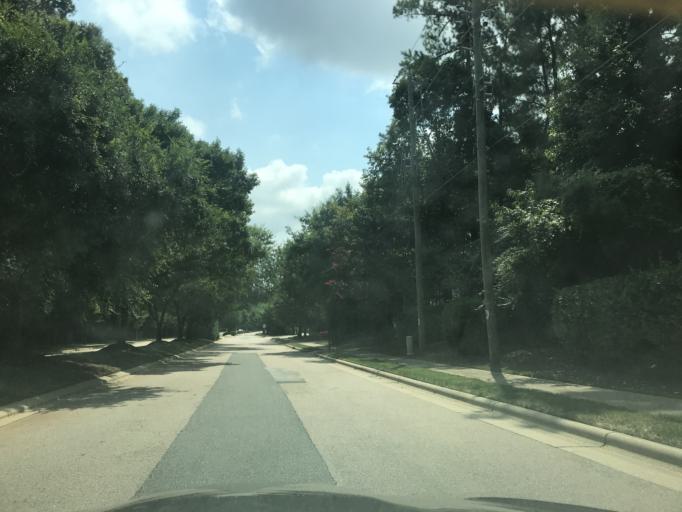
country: US
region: North Carolina
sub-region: Wake County
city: Wake Forest
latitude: 35.9252
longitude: -78.5818
